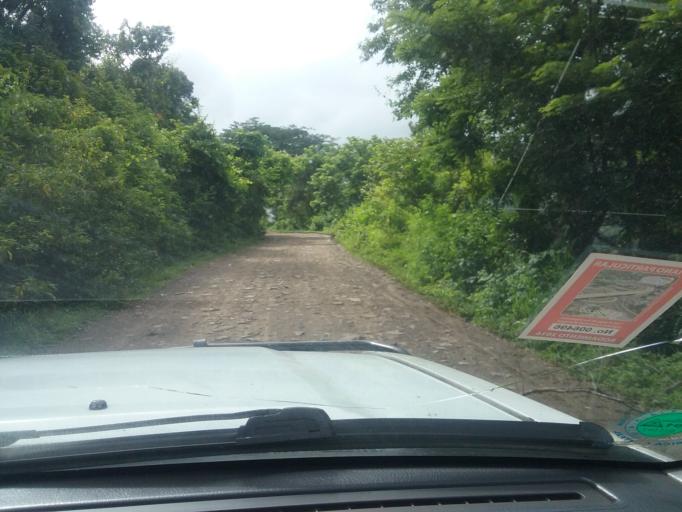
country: NI
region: Matagalpa
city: Matagalpa
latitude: 12.8717
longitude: -85.9526
